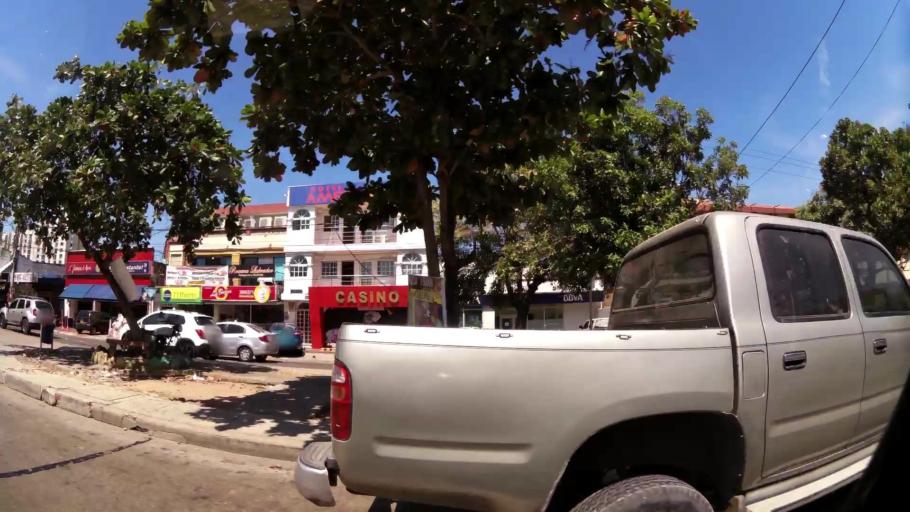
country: CO
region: Atlantico
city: Barranquilla
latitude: 10.9851
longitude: -74.8103
